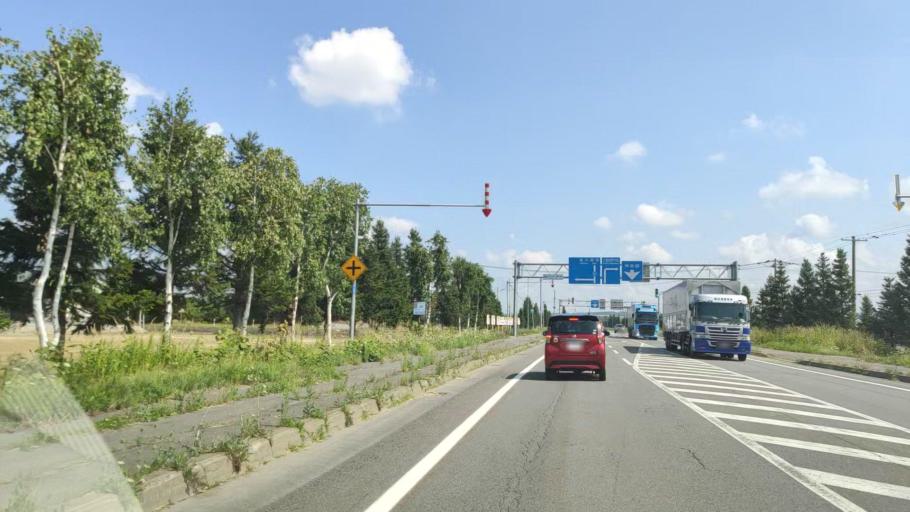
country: JP
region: Hokkaido
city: Shimo-furano
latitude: 43.4748
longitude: 142.4553
